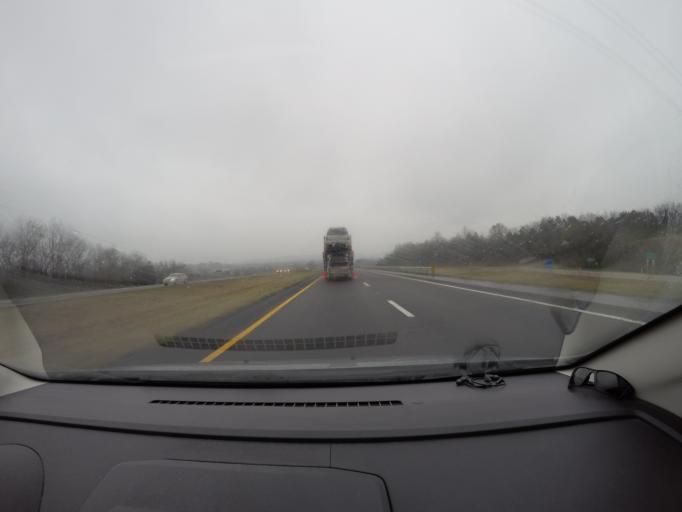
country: US
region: Tennessee
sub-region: Rutherford County
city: Plainview
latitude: 35.6264
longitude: -86.2438
